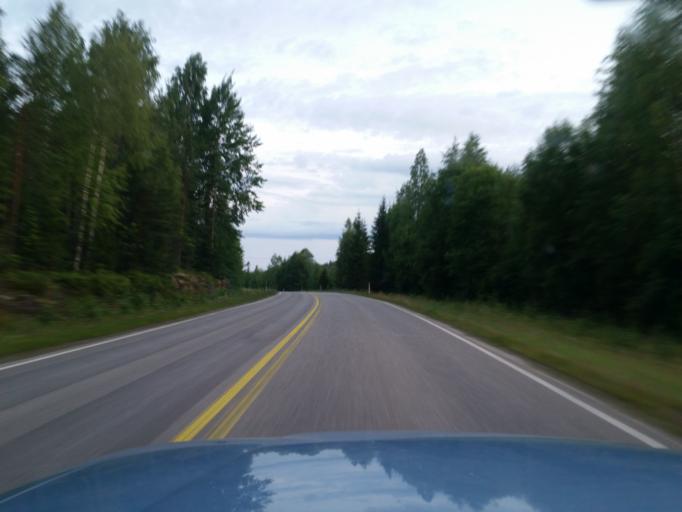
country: FI
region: Southern Savonia
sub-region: Savonlinna
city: Sulkava
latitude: 61.8282
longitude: 28.4418
